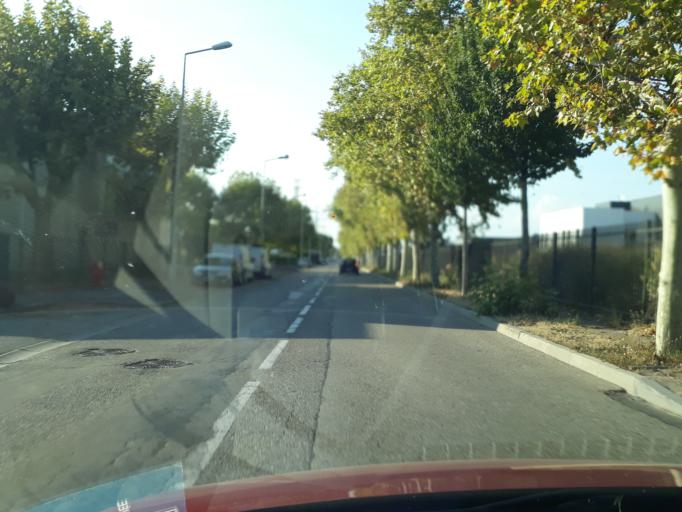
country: FR
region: Rhone-Alpes
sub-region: Departement du Rhone
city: Bron
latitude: 45.7067
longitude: 4.9116
